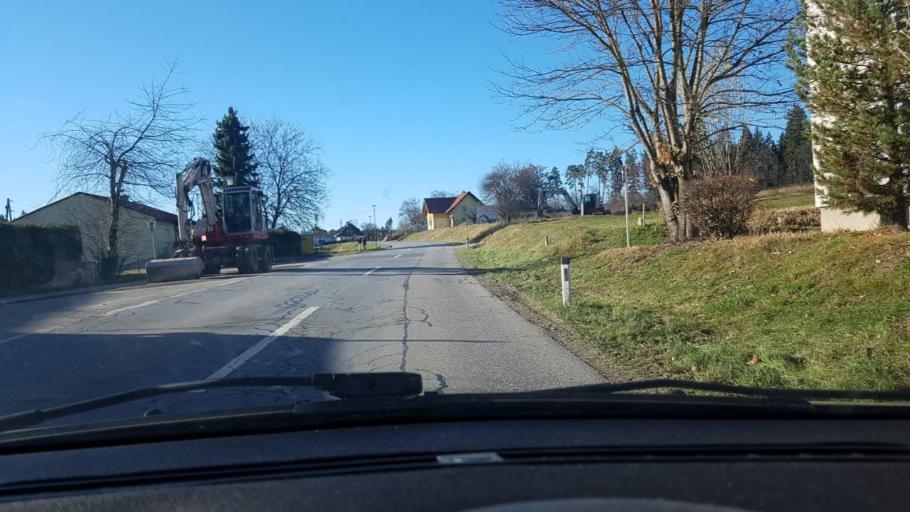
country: AT
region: Carinthia
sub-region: Politischer Bezirk Villach Land
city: Velden am Woerthersee
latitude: 46.6019
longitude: 14.0424
